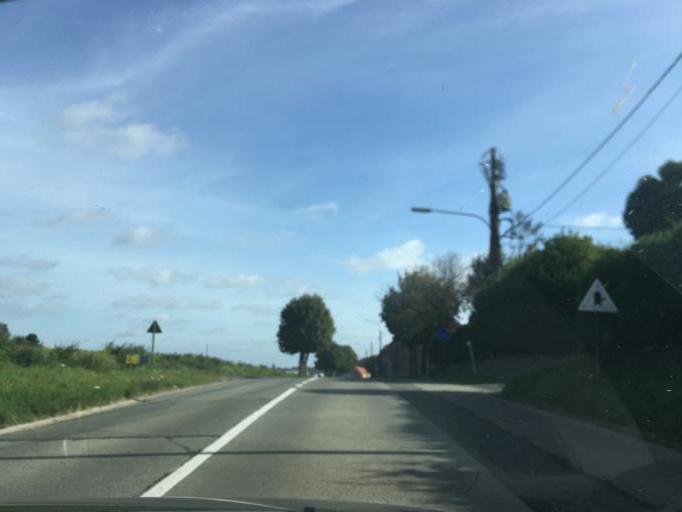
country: BE
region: Flanders
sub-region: Provincie West-Vlaanderen
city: Moorslede
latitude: 50.8812
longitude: 3.0325
